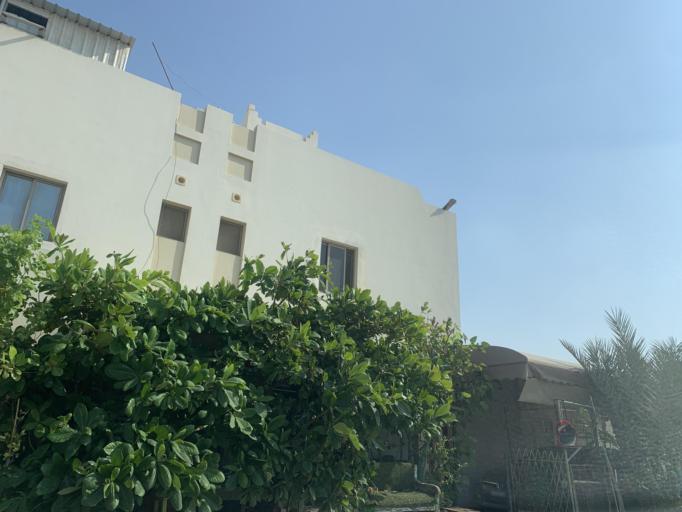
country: BH
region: Central Governorate
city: Madinat Hamad
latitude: 26.1236
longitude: 50.4886
